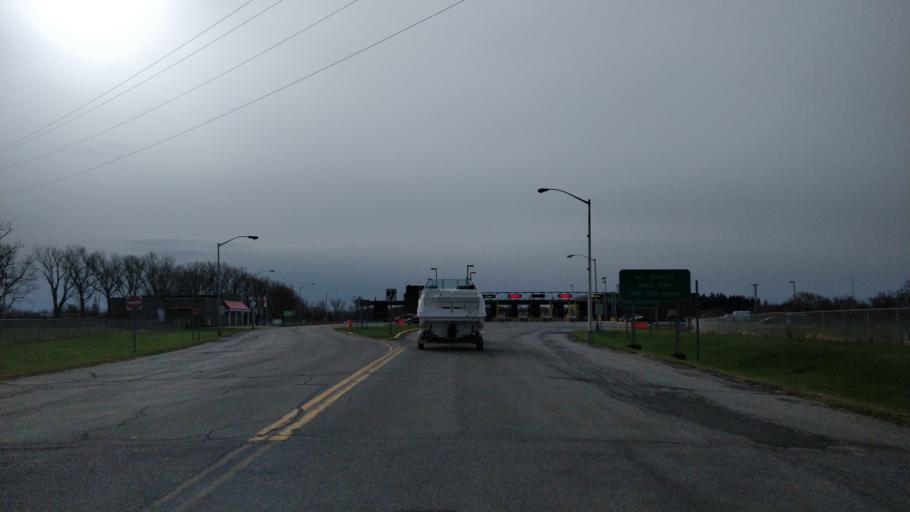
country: US
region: New York
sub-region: St. Lawrence County
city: Ogdensburg
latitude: 44.7238
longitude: -75.4548
